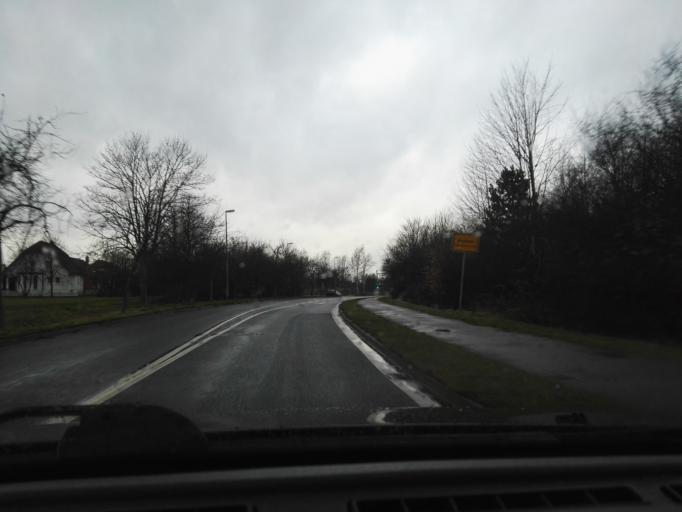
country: DE
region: Lower Saxony
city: Leiferde
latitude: 52.2306
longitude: 10.4897
